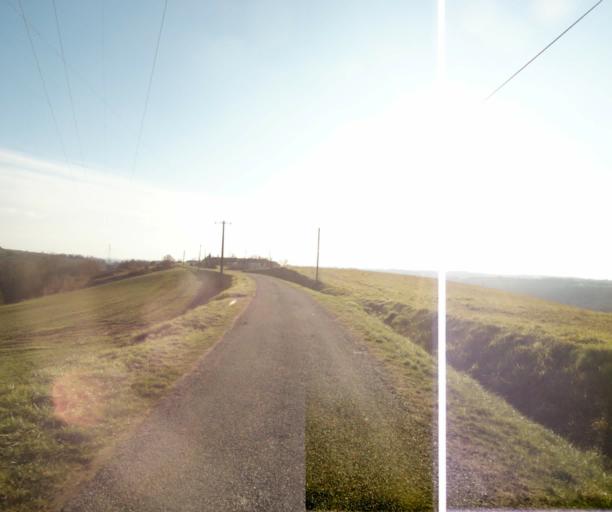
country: FR
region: Midi-Pyrenees
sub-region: Departement du Tarn-et-Garonne
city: Moissac
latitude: 44.1422
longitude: 1.1117
